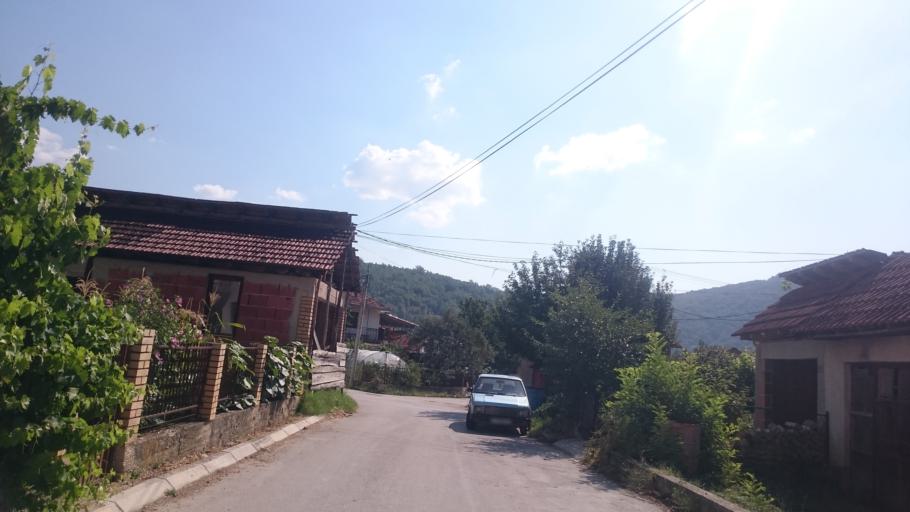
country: MK
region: Makedonski Brod
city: Makedonski Brod
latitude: 41.5129
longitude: 21.2187
